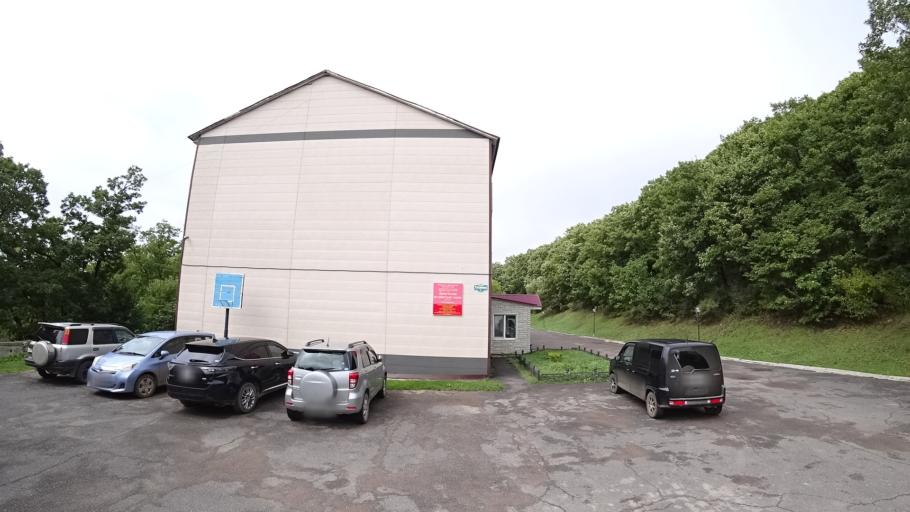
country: RU
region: Primorskiy
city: Monastyrishche
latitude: 44.1695
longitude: 132.5381
